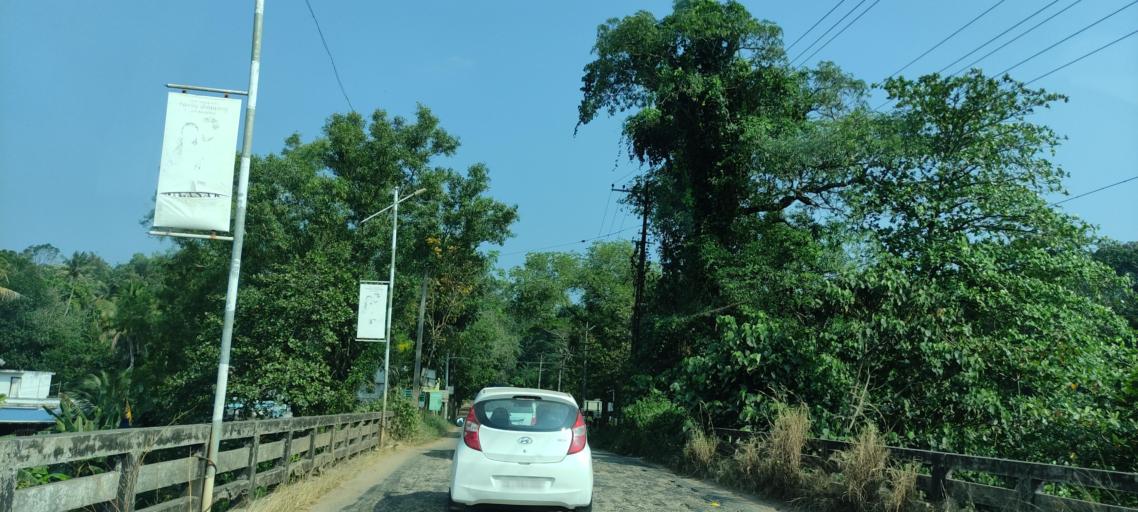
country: IN
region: Kerala
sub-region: Kollam
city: Panmana
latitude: 9.0477
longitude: 76.5703
